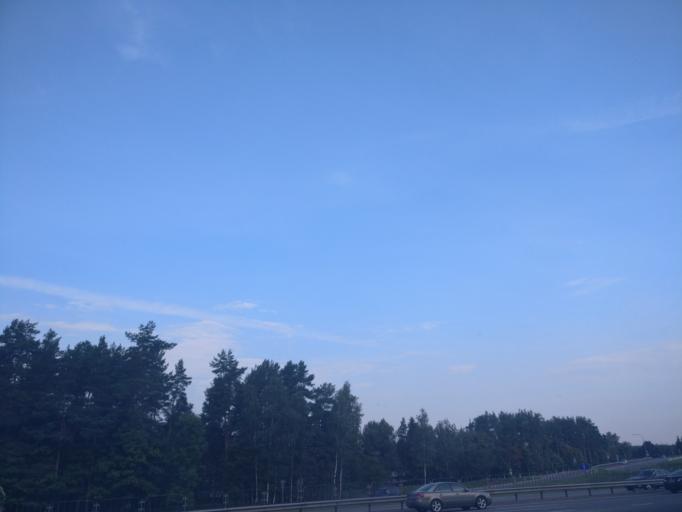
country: BY
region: Minsk
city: Borovlyany
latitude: 53.9639
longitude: 27.6425
